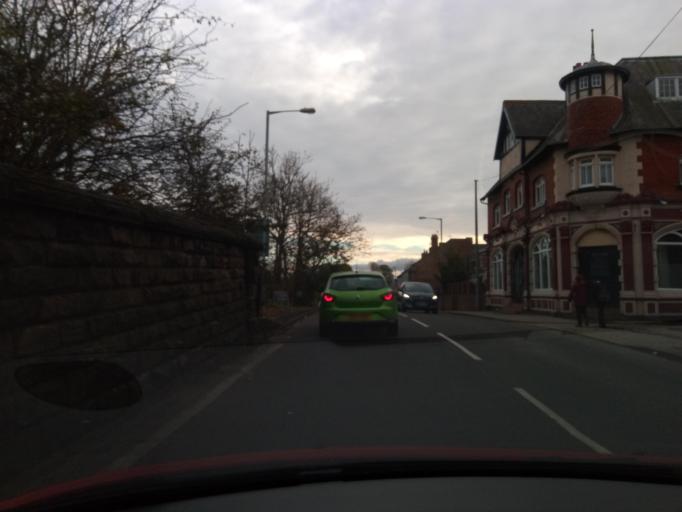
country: GB
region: England
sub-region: County Durham
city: Bishop Auckland
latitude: 54.6565
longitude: -1.6705
